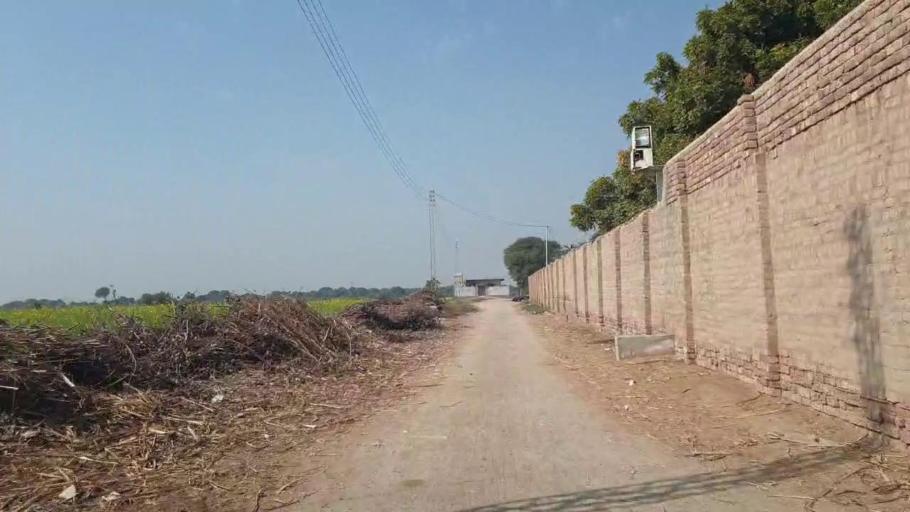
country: PK
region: Sindh
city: Chambar
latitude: 25.3073
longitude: 68.8036
